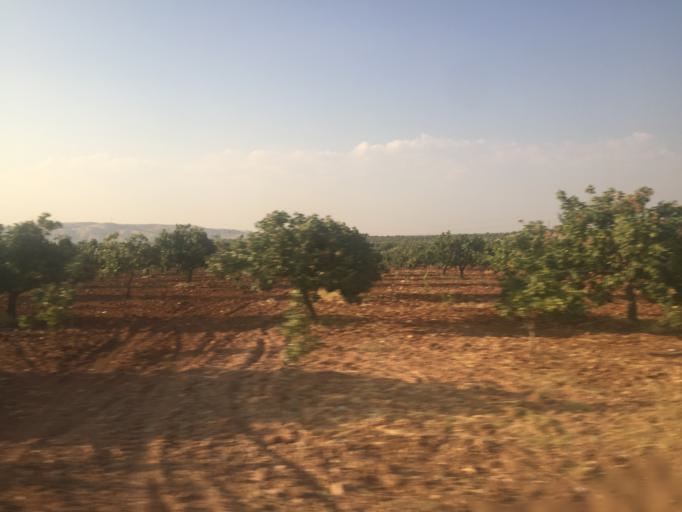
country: TR
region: Gaziantep
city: Nizip
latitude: 37.0142
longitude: 37.8399
